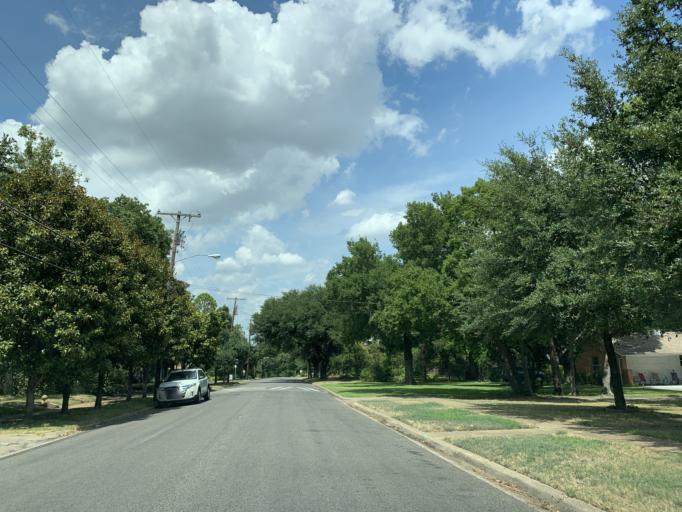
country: US
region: Texas
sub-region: Dallas County
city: Cockrell Hill
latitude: 32.7513
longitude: -96.8546
